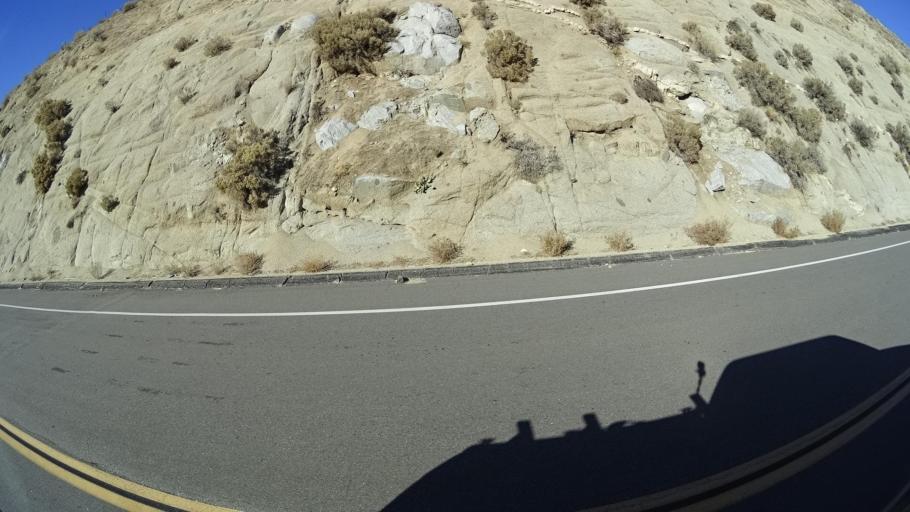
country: US
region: California
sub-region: Kern County
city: Weldon
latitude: 35.6723
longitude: -118.3486
